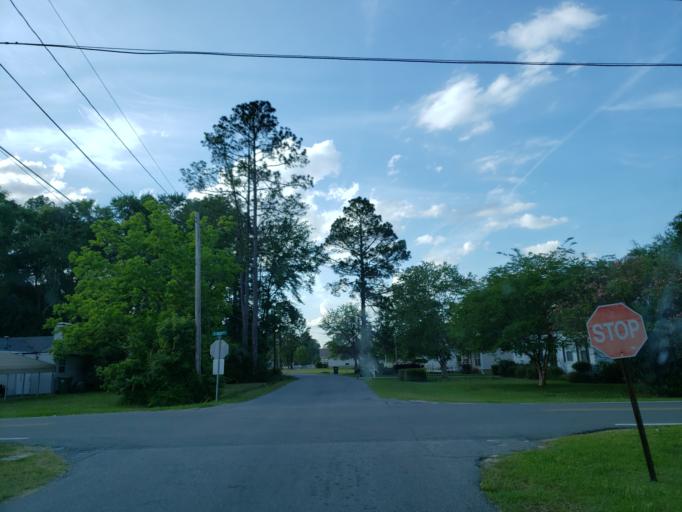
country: US
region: Georgia
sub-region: Cook County
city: Adel
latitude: 31.1358
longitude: -83.4169
